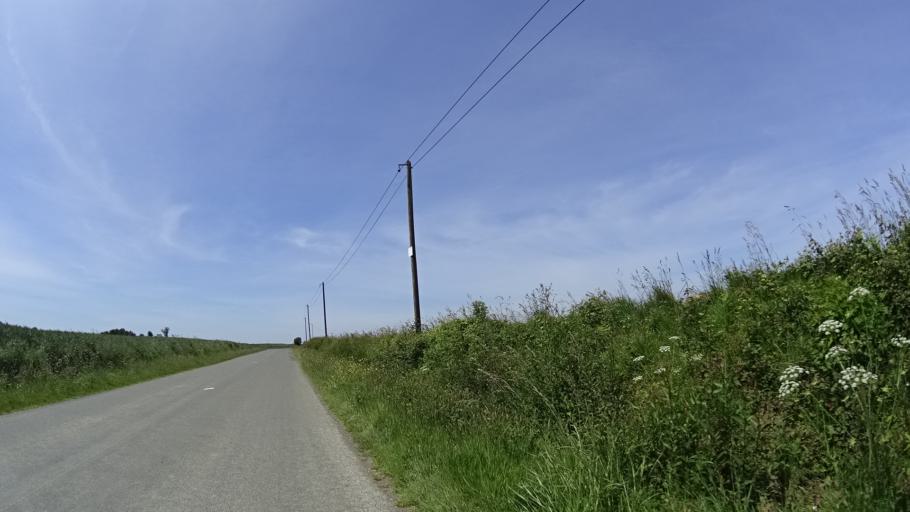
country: FR
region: Brittany
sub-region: Departement d'Ille-et-Vilaine
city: Romille
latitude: 48.1931
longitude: -1.8785
